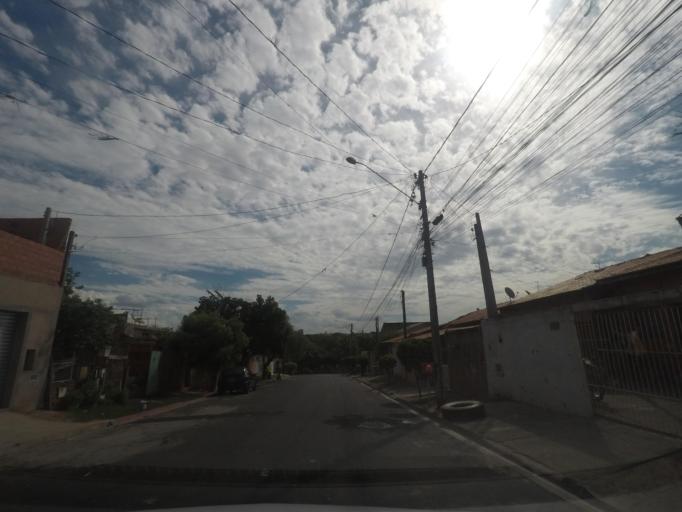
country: BR
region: Sao Paulo
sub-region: Sumare
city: Sumare
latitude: -22.8074
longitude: -47.2749
